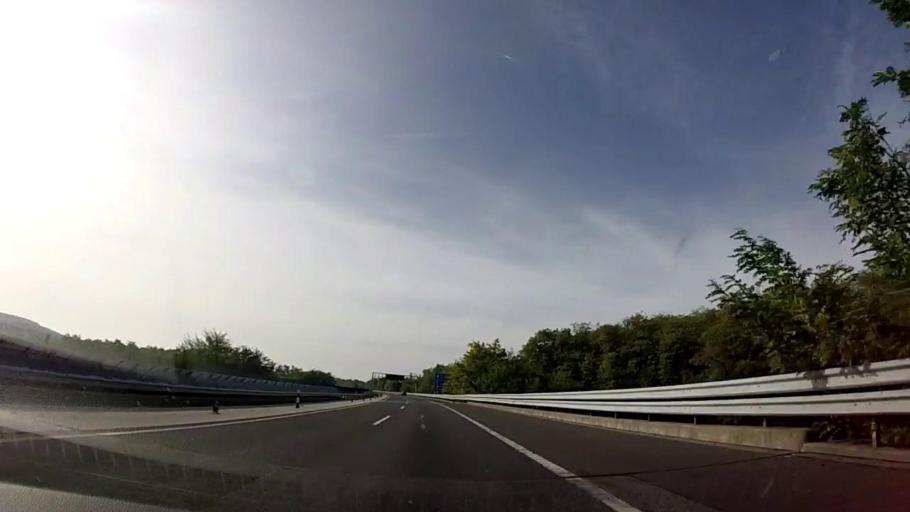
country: HU
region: Somogy
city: Balatonfoldvar
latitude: 46.8279
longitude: 17.9336
